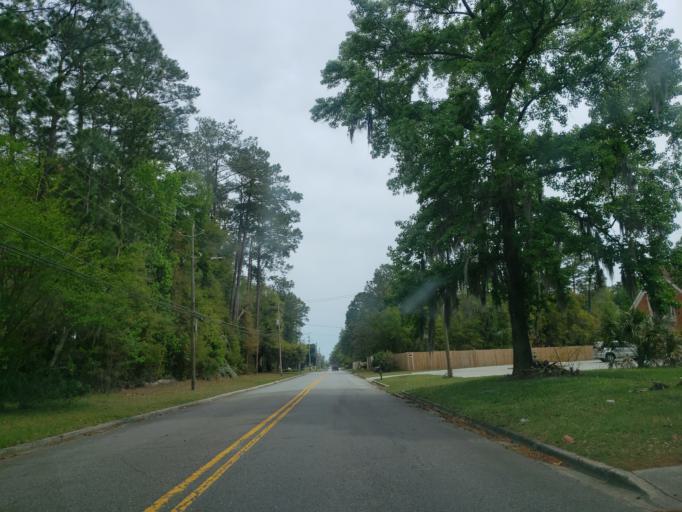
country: US
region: Georgia
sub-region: Chatham County
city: Montgomery
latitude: 31.9904
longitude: -81.1628
